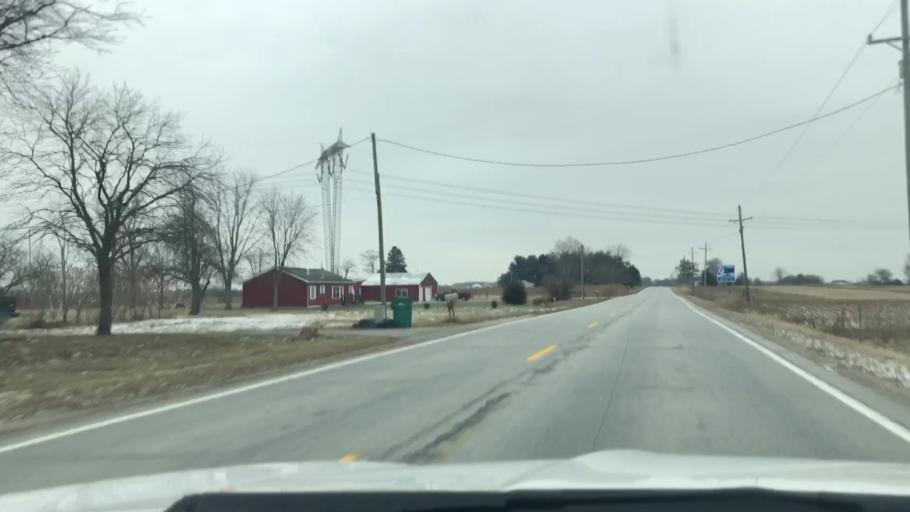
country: US
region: Indiana
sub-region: Fulton County
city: Rochester
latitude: 41.0545
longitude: -86.1445
